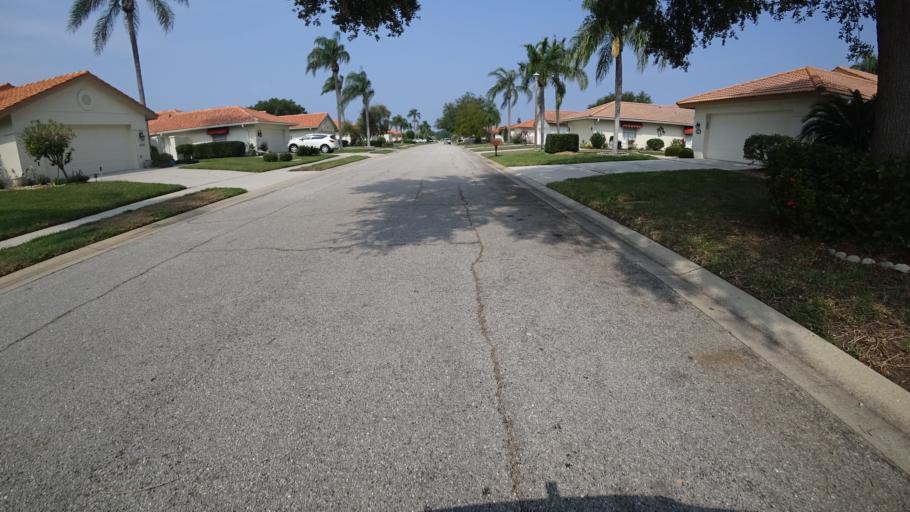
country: US
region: Florida
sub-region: Manatee County
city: Samoset
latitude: 27.4589
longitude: -82.5083
